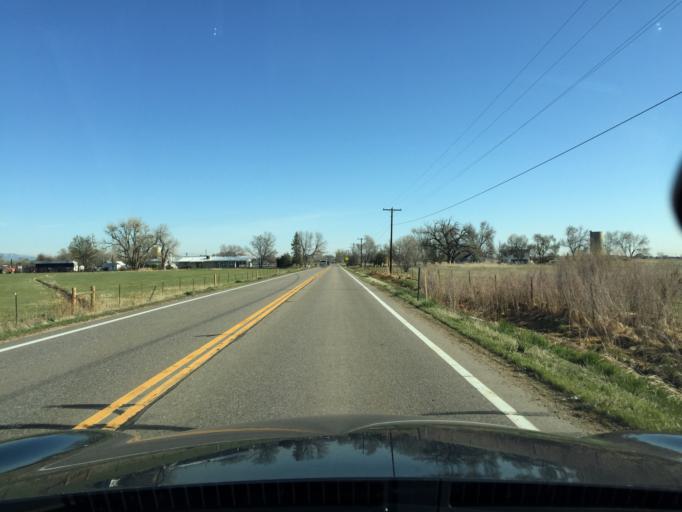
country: US
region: Colorado
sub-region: Boulder County
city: Erie
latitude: 40.0802
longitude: -105.0554
